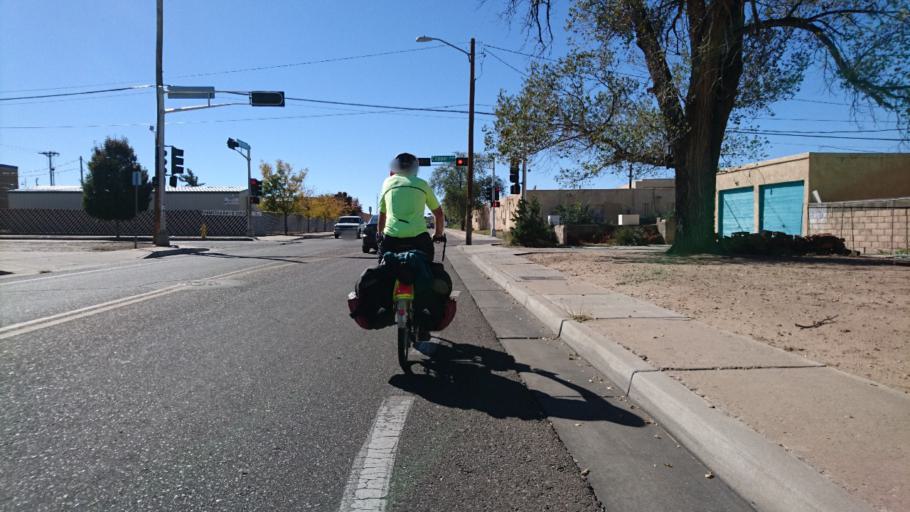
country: US
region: New Mexico
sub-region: Bernalillo County
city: Albuquerque
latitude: 35.0805
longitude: -106.5954
